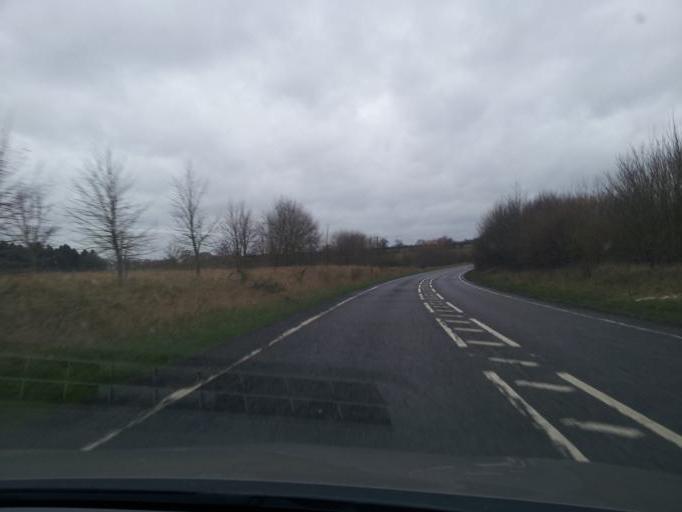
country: GB
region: England
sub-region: Suffolk
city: Botesdale
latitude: 52.3324
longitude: 0.9891
